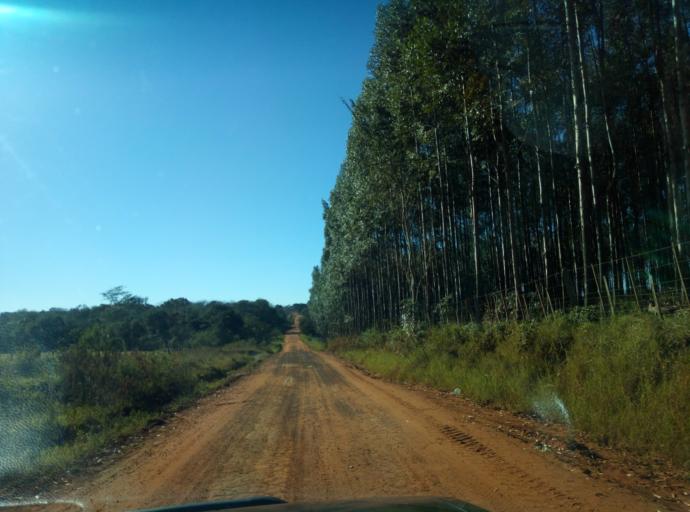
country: PY
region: Caaguazu
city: Doctor Cecilio Baez
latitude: -25.1632
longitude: -56.2608
